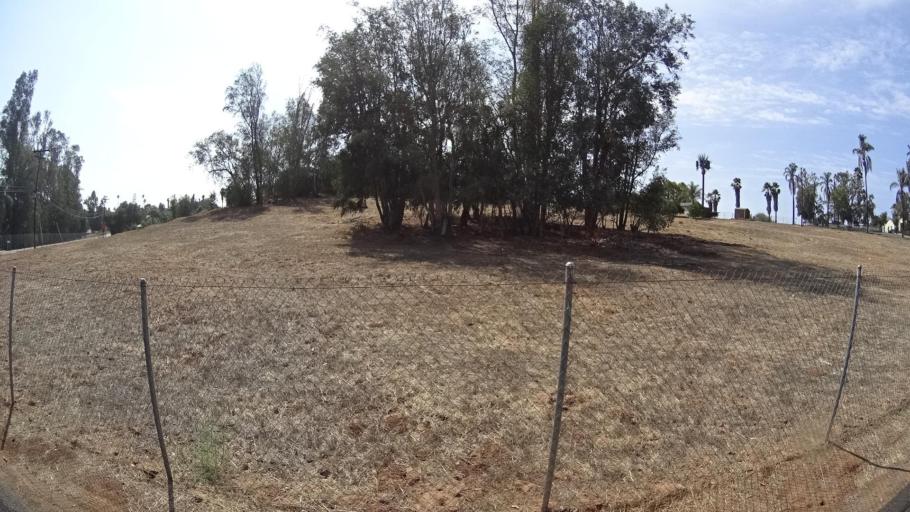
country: US
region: California
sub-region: San Diego County
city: Escondido
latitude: 33.1099
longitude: -117.0439
